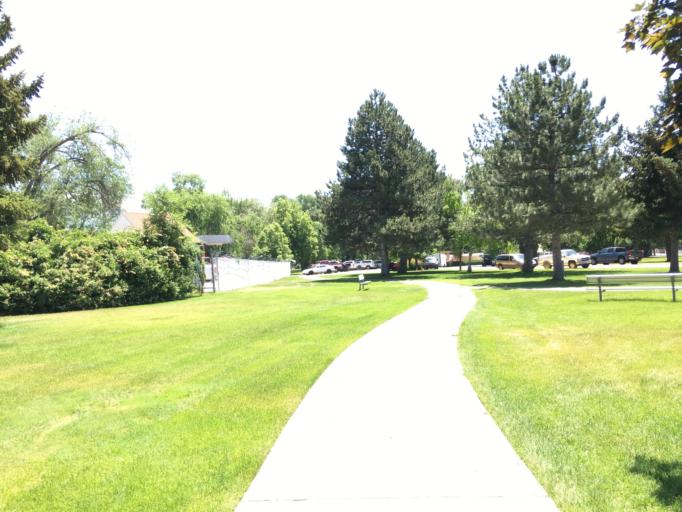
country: US
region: Utah
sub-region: Davis County
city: Layton
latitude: 41.0688
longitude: -111.9597
